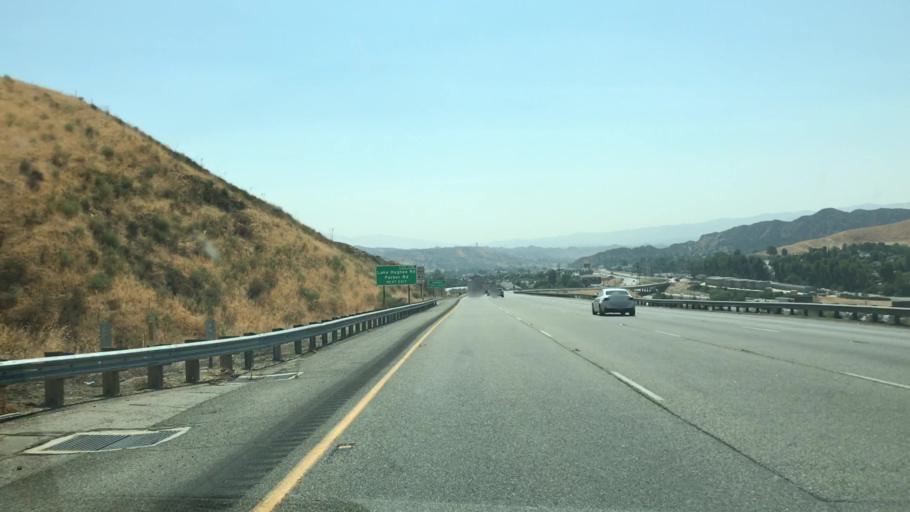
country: US
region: California
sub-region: Los Angeles County
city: Castaic
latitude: 34.5099
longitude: -118.6309
